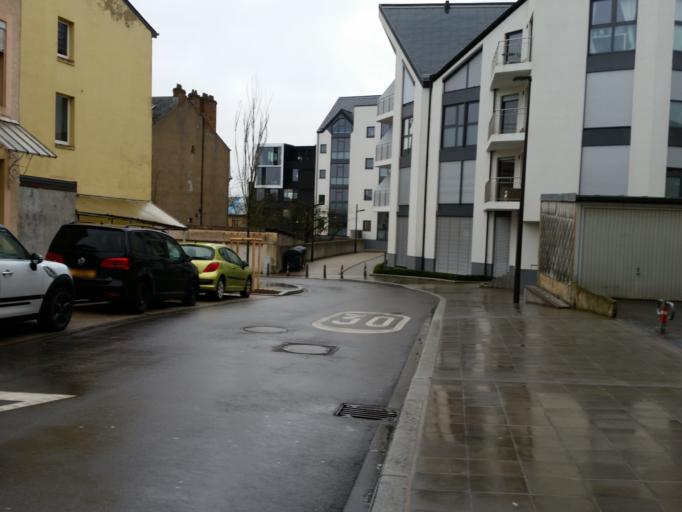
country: LU
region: Luxembourg
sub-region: Canton de Luxembourg
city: Luxembourg
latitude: 49.6032
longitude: 6.1380
